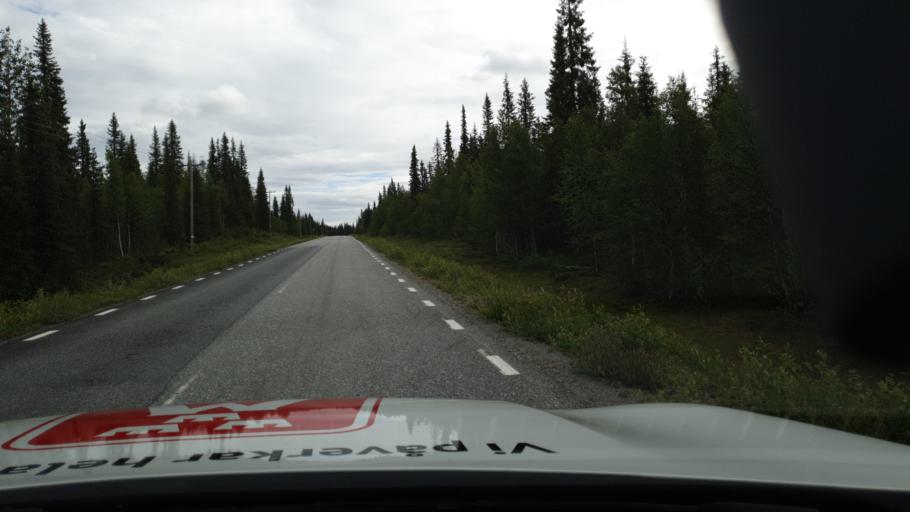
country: SE
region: Vaesterbotten
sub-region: Storumans Kommun
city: Fristad
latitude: 65.4226
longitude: 16.6284
